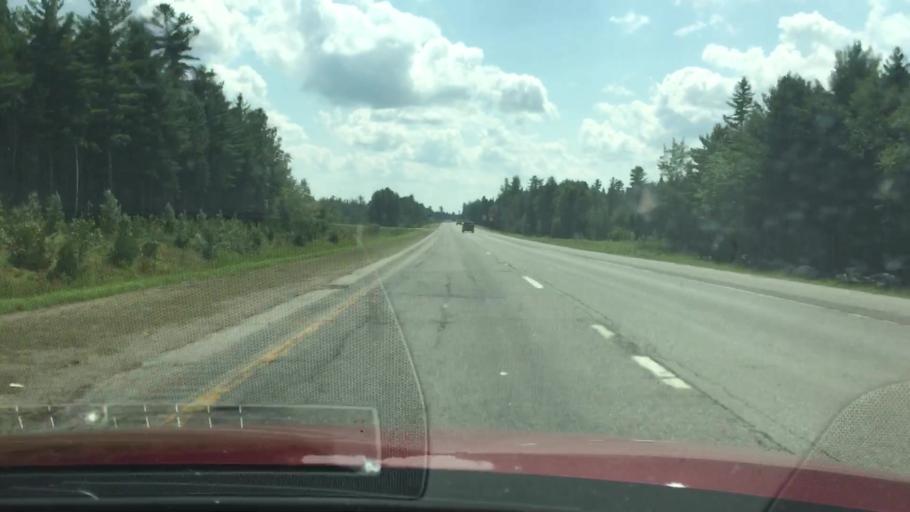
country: US
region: Maine
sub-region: Penobscot County
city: Medway
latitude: 45.5879
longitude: -68.5429
